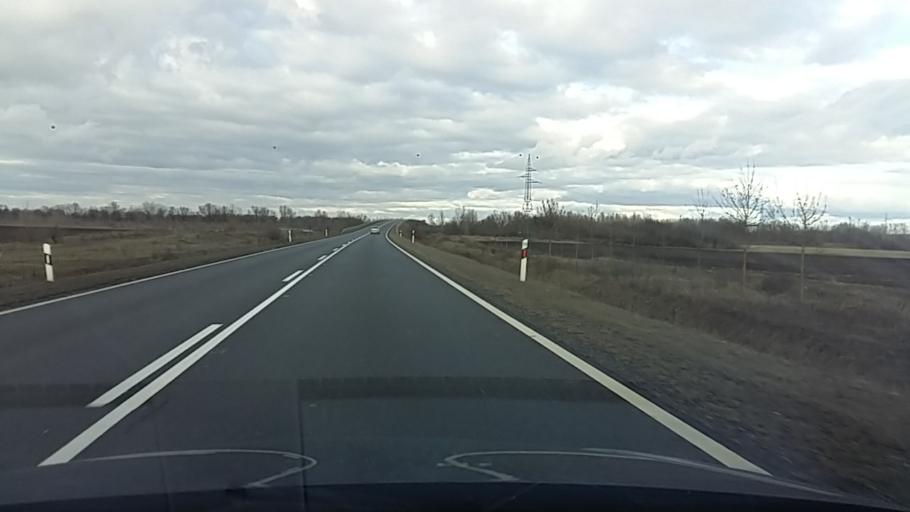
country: HU
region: Szabolcs-Szatmar-Bereg
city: Nyirpazony
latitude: 47.9411
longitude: 21.8186
